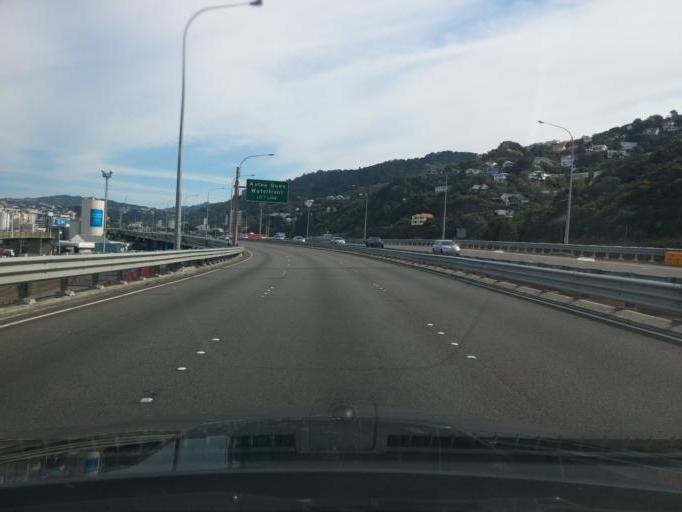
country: NZ
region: Wellington
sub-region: Wellington City
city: Wellington
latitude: -41.2623
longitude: 174.7890
